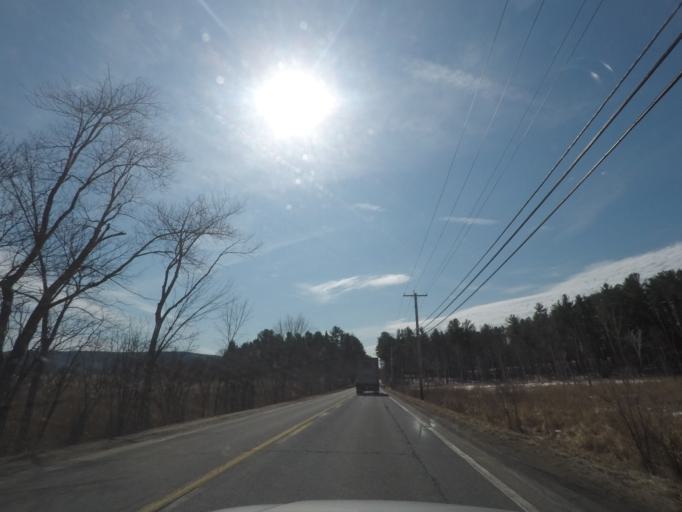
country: US
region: Massachusetts
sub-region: Berkshire County
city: Stockbridge
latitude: 42.2897
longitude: -73.2979
